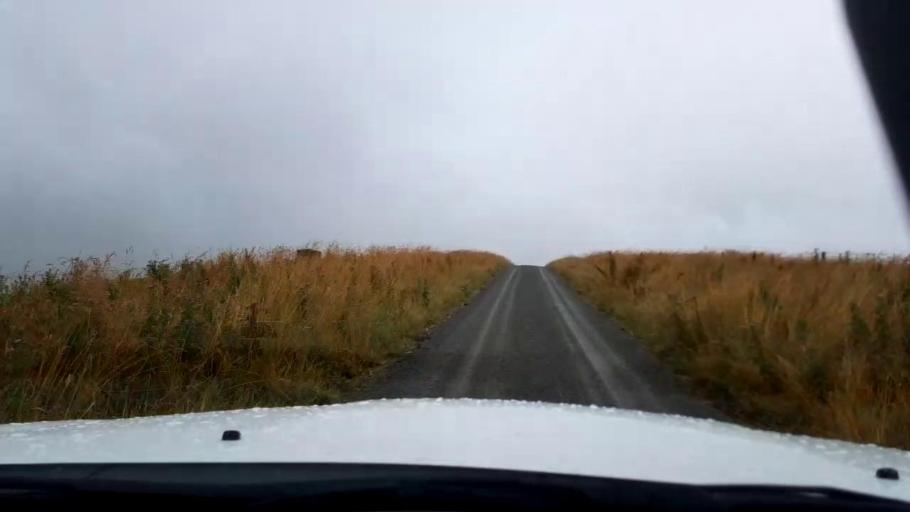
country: NZ
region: Canterbury
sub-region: Timaru District
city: Pleasant Point
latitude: -44.1751
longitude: 171.0918
